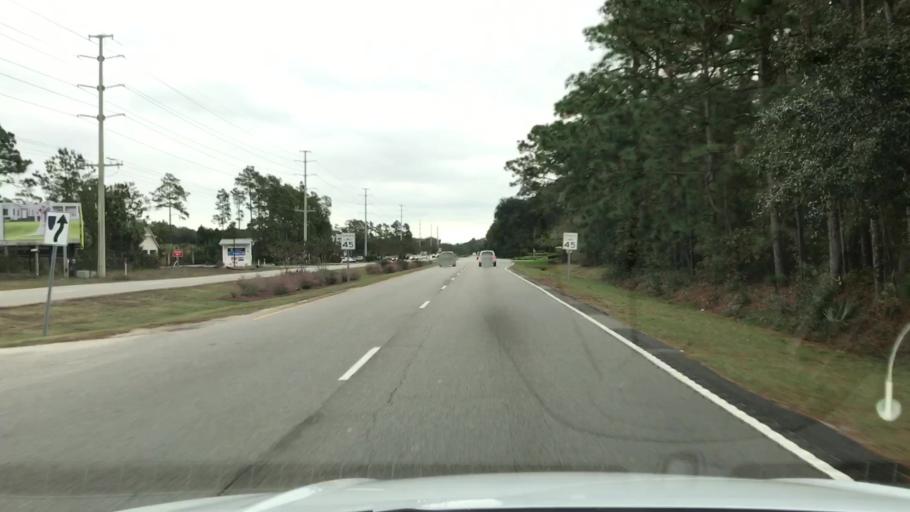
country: US
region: South Carolina
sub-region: Georgetown County
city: Georgetown
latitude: 33.4248
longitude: -79.1603
